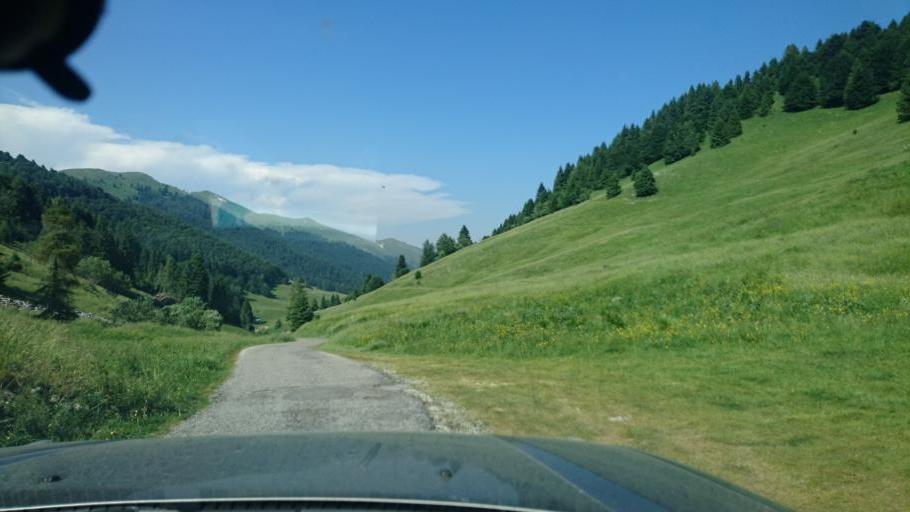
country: IT
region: Veneto
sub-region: Provincia di Treviso
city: Crespano del Grappa
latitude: 45.8858
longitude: 11.8167
